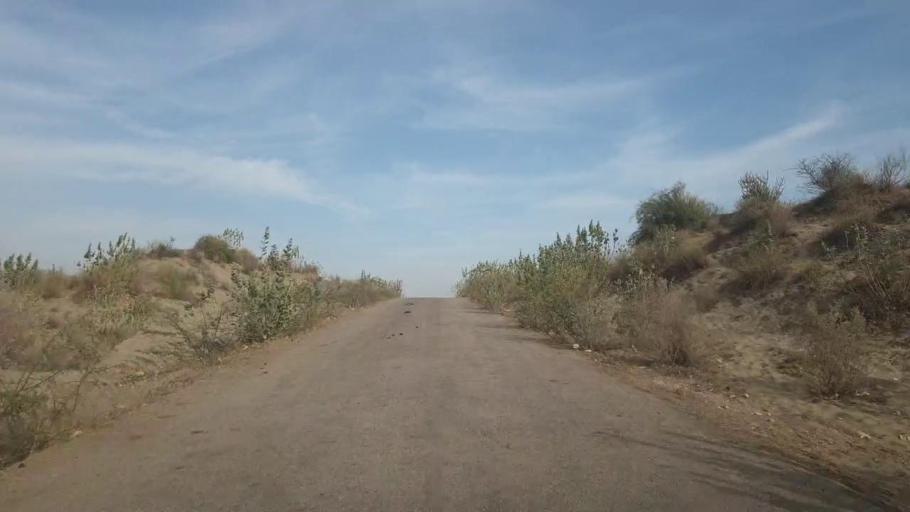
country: PK
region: Sindh
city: Nabisar
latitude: 25.0531
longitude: 69.6915
